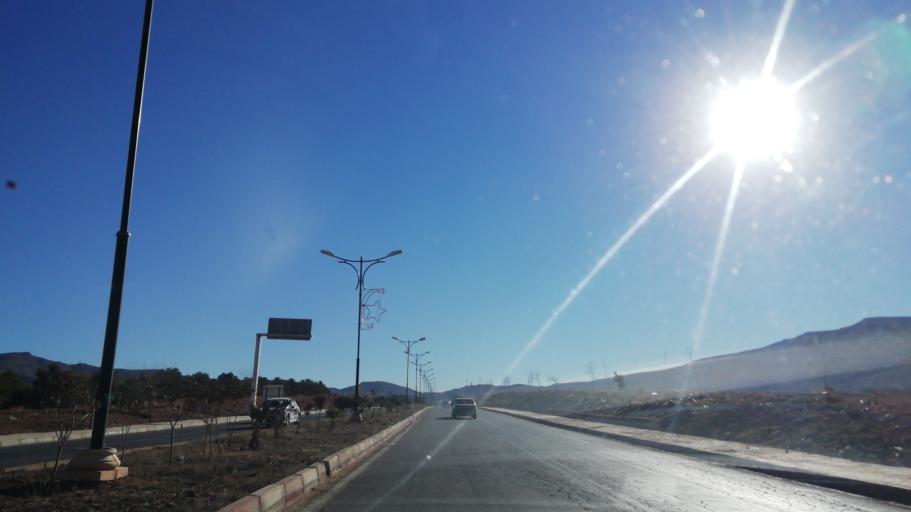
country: DZ
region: El Bayadh
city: El Bayadh
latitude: 33.6608
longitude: 1.0580
